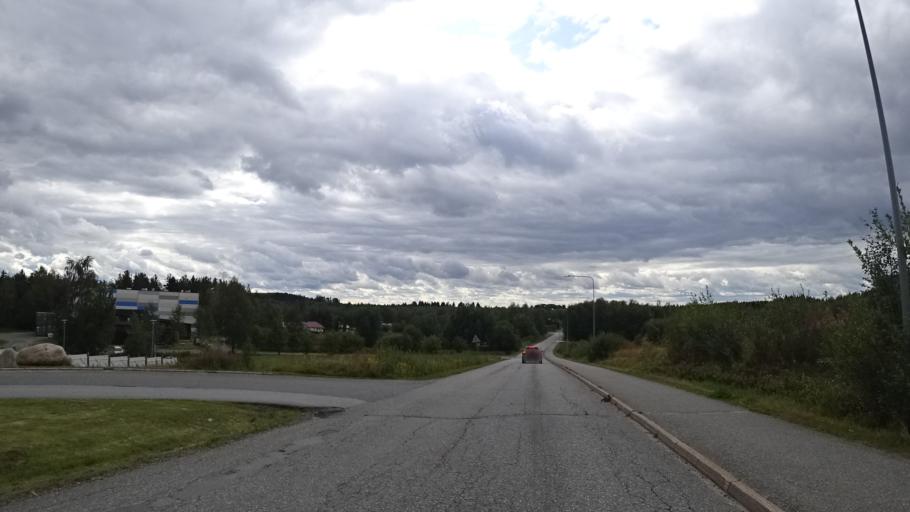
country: FI
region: North Karelia
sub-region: Joensuu
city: Ilomantsi
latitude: 62.6669
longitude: 30.9270
